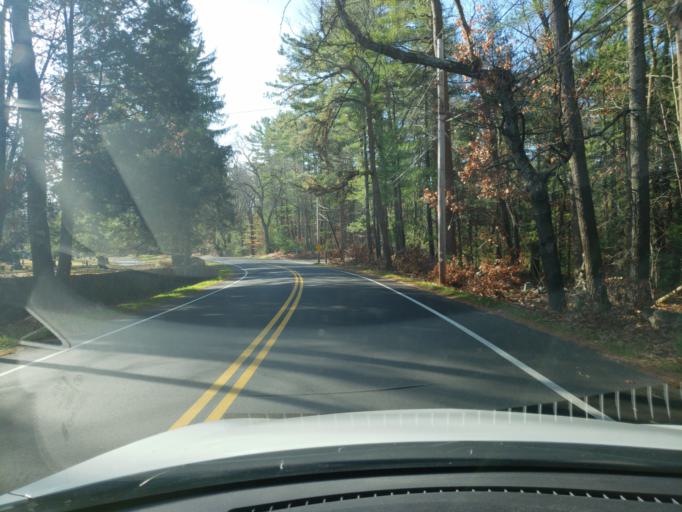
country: US
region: Massachusetts
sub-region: Essex County
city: Andover
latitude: 42.6393
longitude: -71.1471
